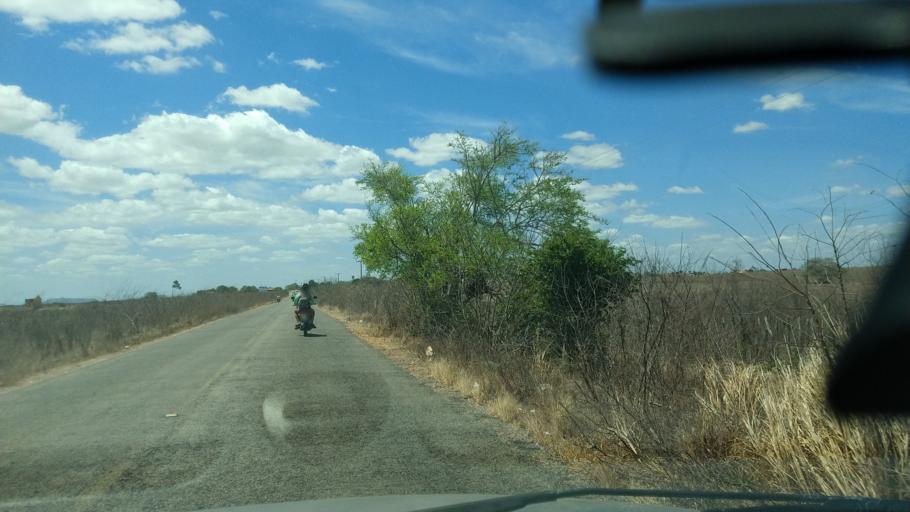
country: BR
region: Rio Grande do Norte
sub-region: Sao Paulo Do Potengi
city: Sao Paulo do Potengi
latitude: -5.9141
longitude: -35.7474
